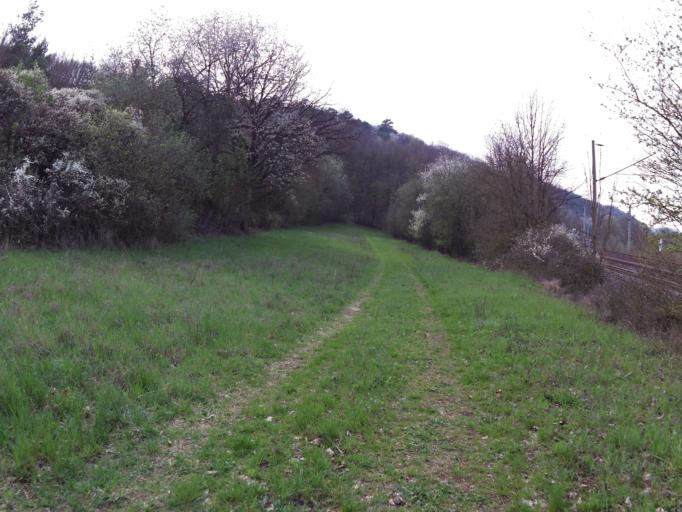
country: DE
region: Bavaria
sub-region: Regierungsbezirk Unterfranken
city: Rottendorf
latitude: 49.7835
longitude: 10.0224
